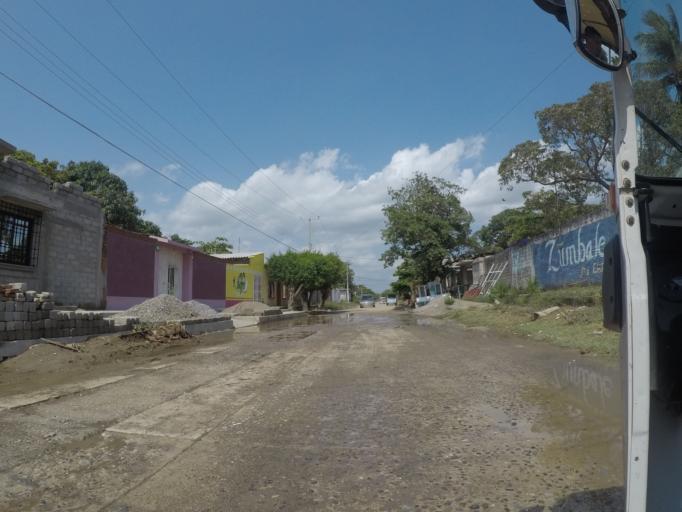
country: MX
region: Oaxaca
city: Union Hidalgo
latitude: 16.4702
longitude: -94.8347
